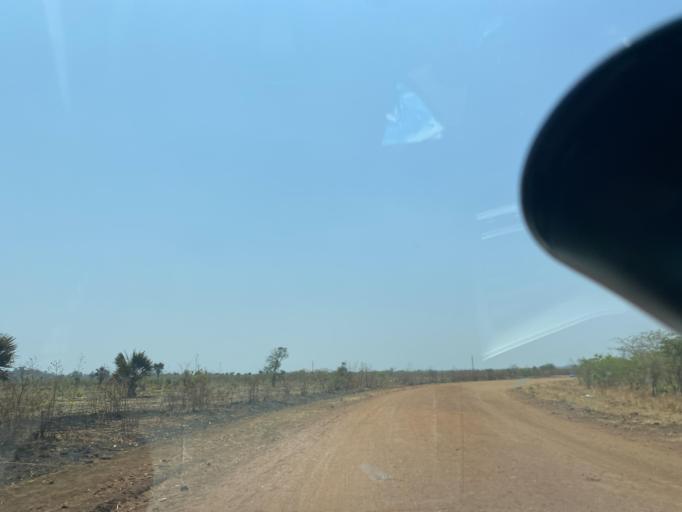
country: ZM
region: Lusaka
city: Lusaka
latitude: -15.4594
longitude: 27.9160
